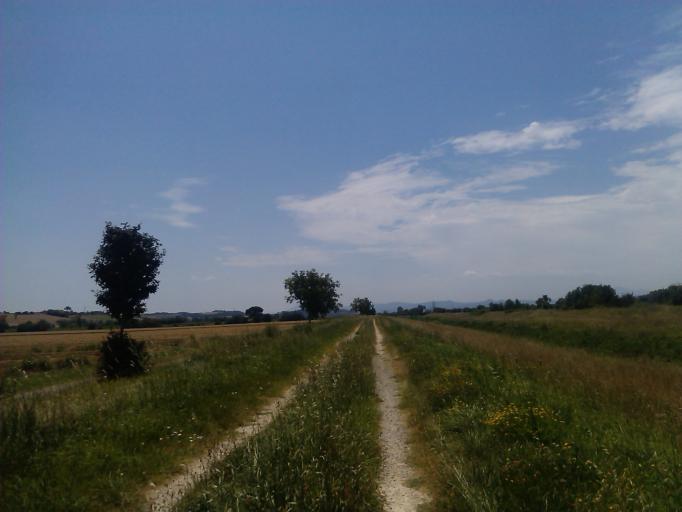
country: IT
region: Tuscany
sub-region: Province of Arezzo
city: Cesa
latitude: 43.2877
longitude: 11.8414
